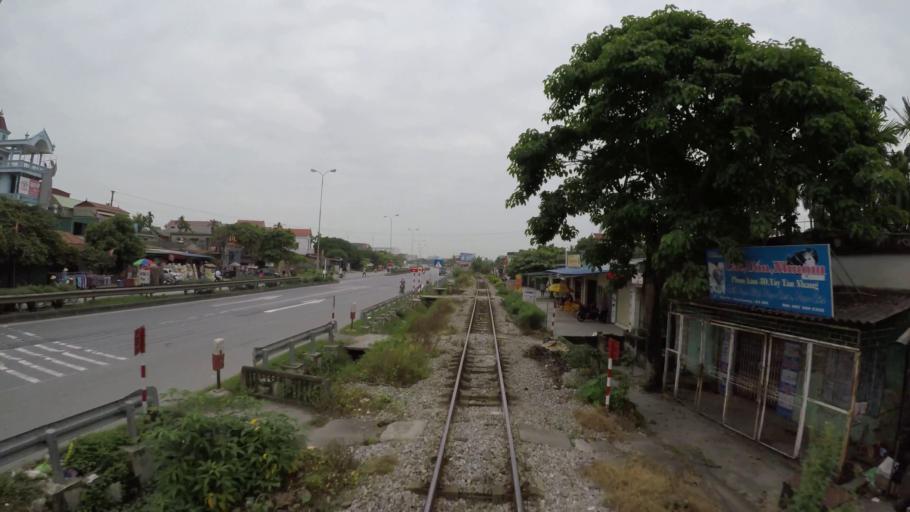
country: VN
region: Hai Duong
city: Phu Thai
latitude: 20.9533
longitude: 106.5304
